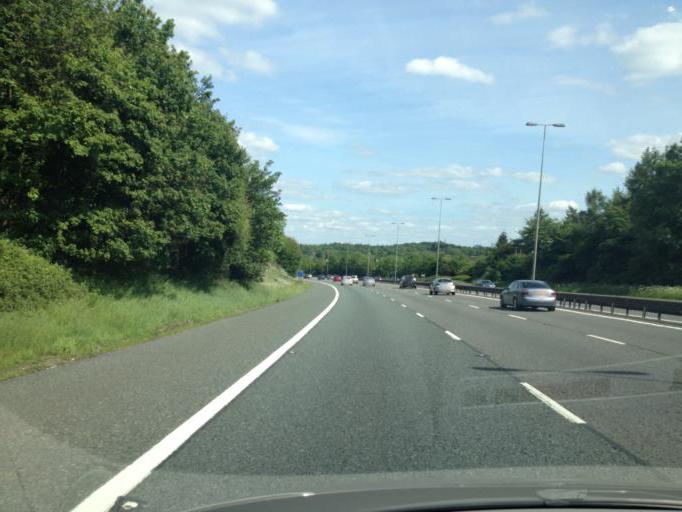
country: GB
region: England
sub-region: Buckinghamshire
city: Stokenchurch
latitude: 51.6259
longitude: -0.8426
